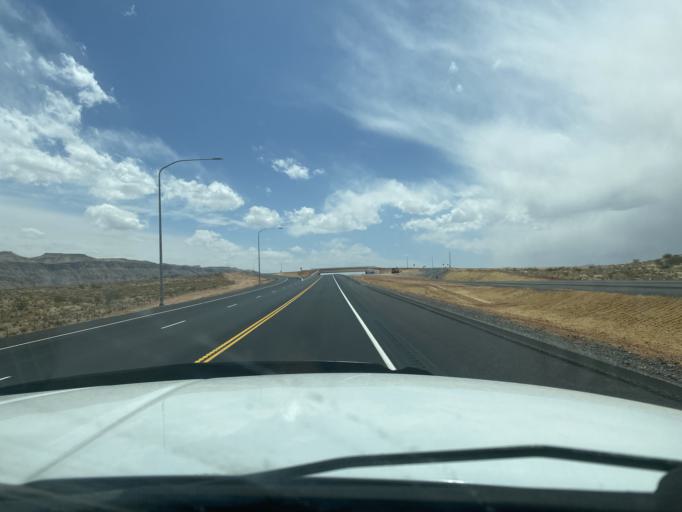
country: US
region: Utah
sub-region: Washington County
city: Hurricane
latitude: 37.1312
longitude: -113.3472
